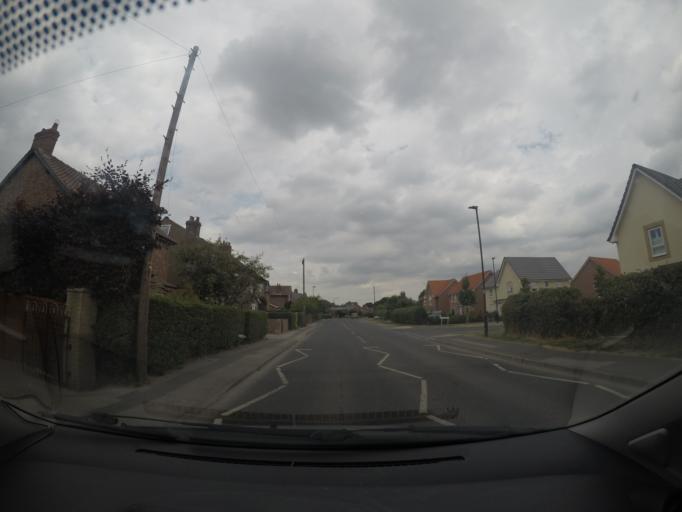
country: GB
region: England
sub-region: City of York
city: Huntington
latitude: 53.9910
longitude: -1.0591
